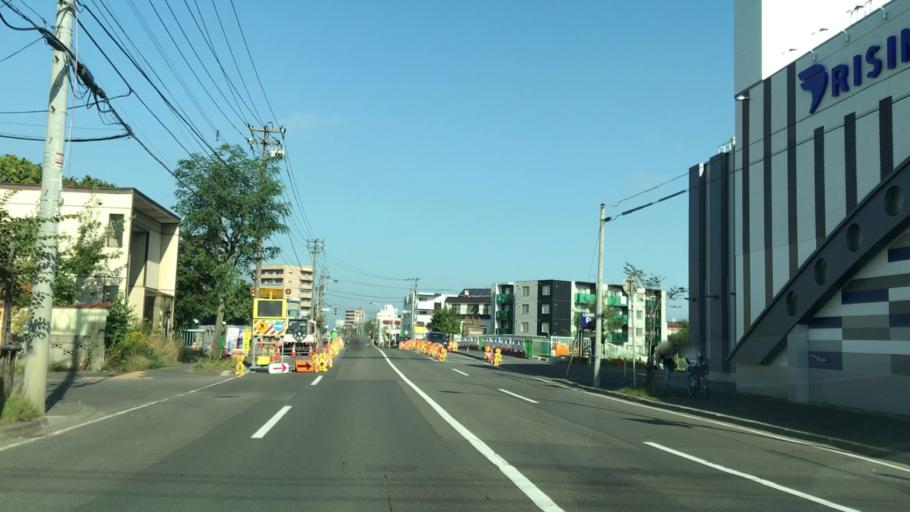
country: JP
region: Hokkaido
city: Sapporo
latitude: 43.0825
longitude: 141.3021
